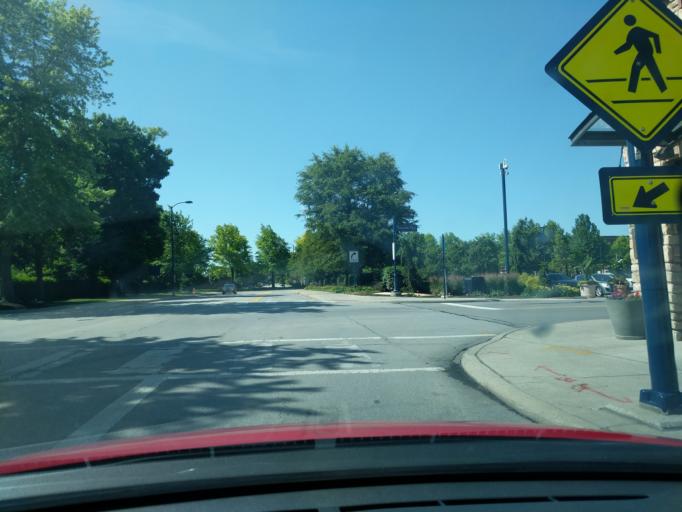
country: US
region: Ohio
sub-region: Franklin County
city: Huber Ridge
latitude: 40.0492
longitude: -82.9132
